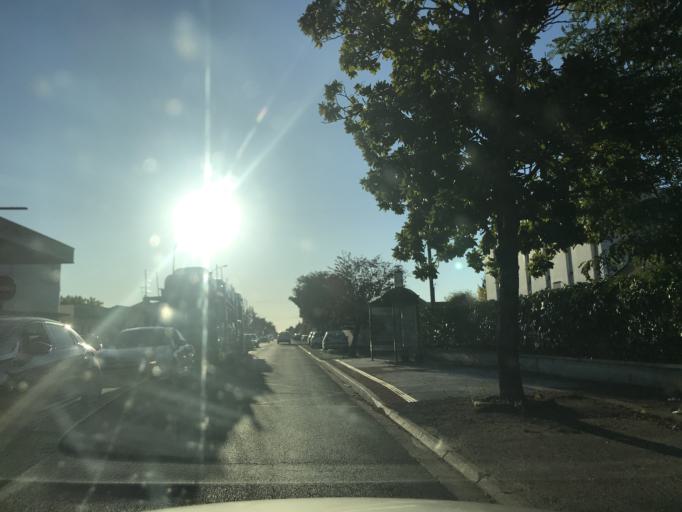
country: FR
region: Aquitaine
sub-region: Departement de la Gironde
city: Mouliets-et-Villemartin
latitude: 44.8544
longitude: -0.0510
